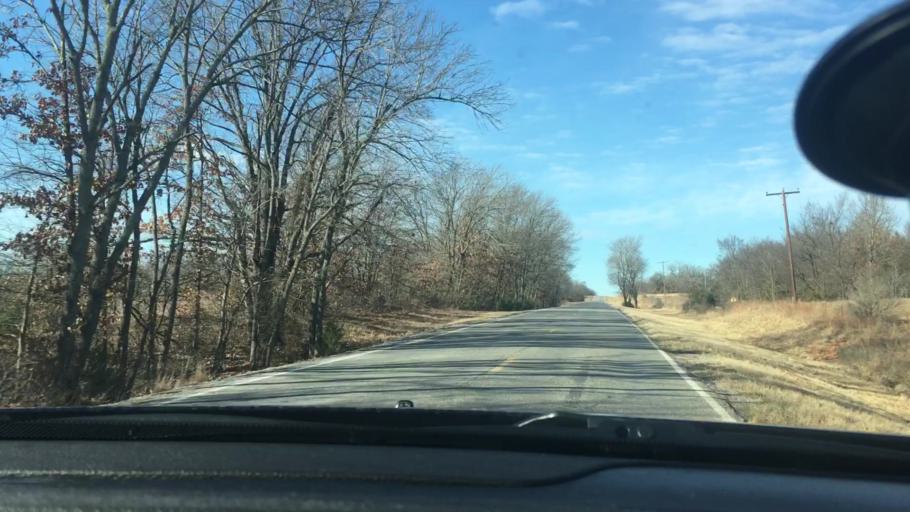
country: US
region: Oklahoma
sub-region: Seminole County
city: Konawa
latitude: 34.9857
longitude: -96.8665
